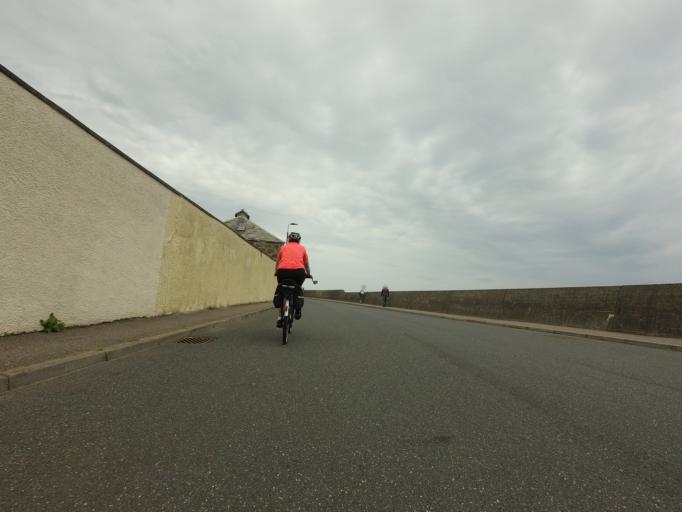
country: GB
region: Scotland
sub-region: Aberdeenshire
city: Banff
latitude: 57.6670
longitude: -2.5207
